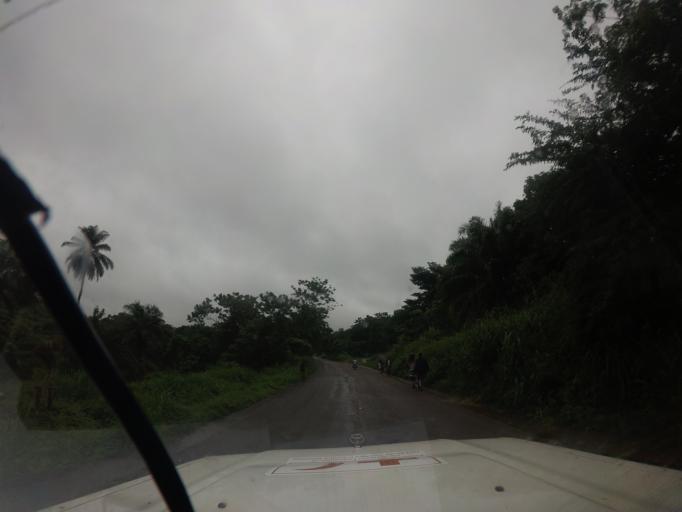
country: SL
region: Northern Province
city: Kabala
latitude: 9.5403
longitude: -11.5781
